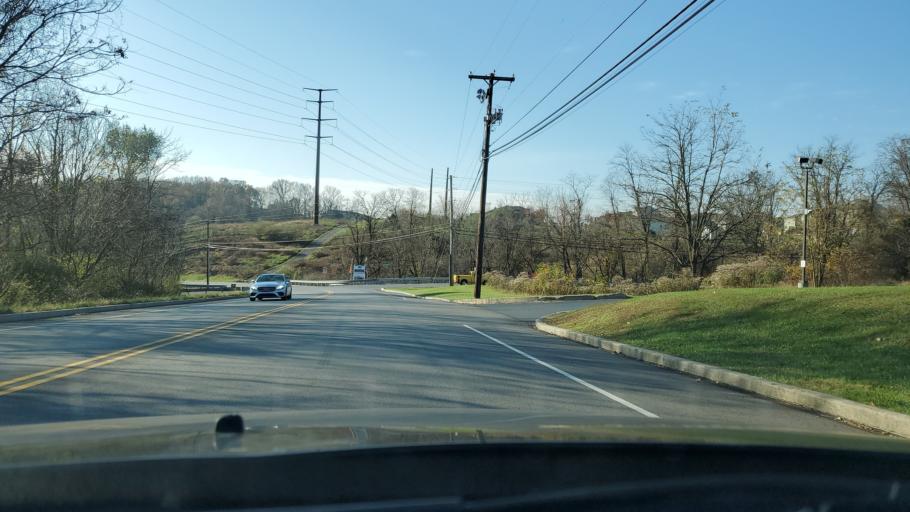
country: US
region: Pennsylvania
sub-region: Cumberland County
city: Mechanicsburg
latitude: 40.1729
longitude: -76.9871
